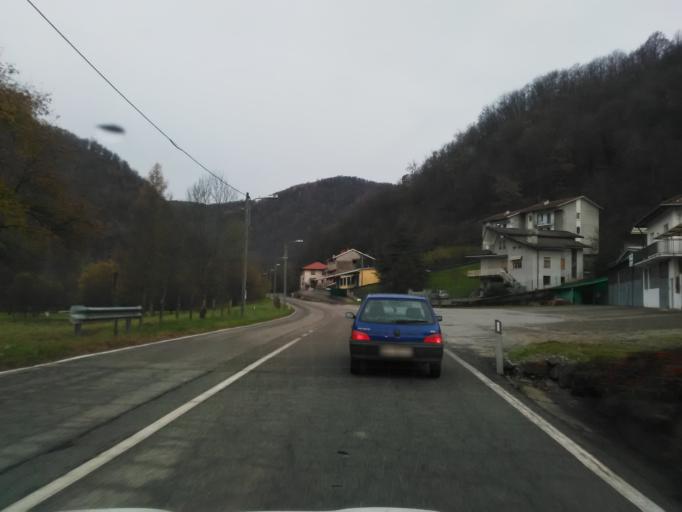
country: IT
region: Piedmont
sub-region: Provincia di Biella
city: Crevacuore
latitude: 45.6796
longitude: 8.2367
